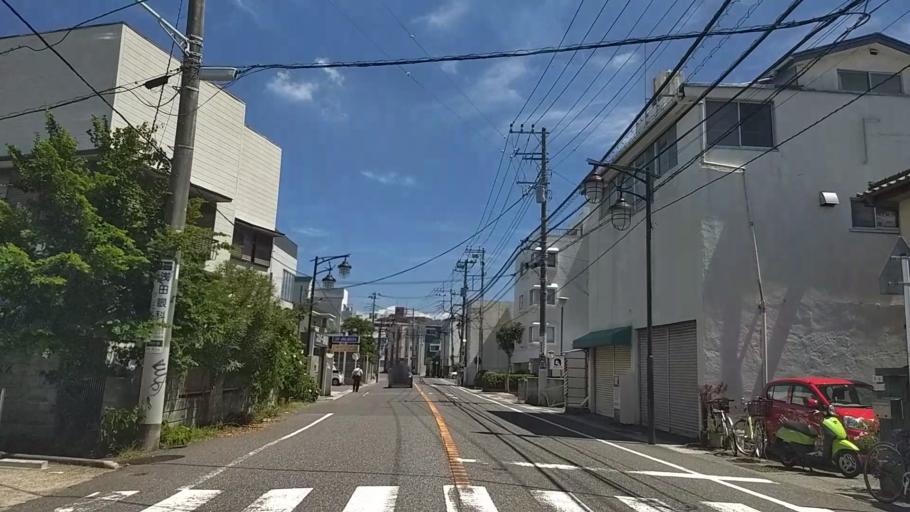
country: JP
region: Kanagawa
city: Zushi
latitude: 35.2978
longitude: 139.5731
